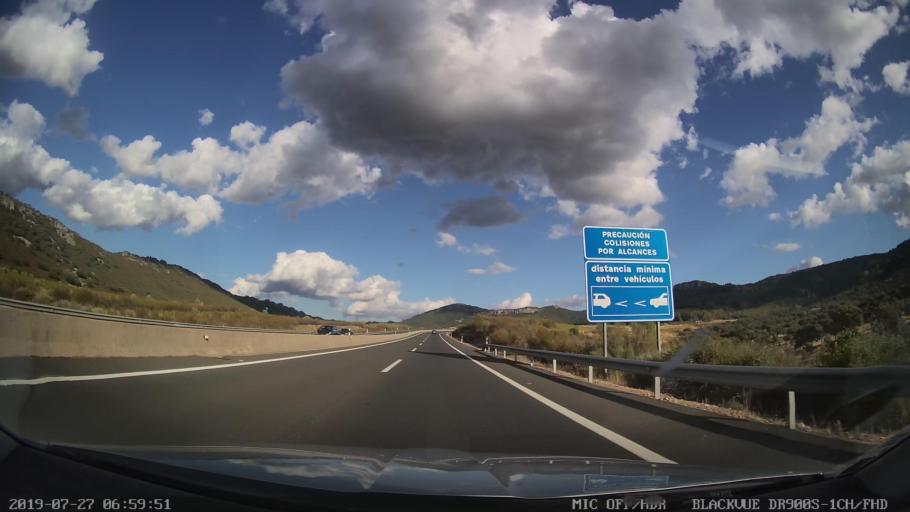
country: ES
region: Extremadura
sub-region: Provincia de Caceres
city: Higuera
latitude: 39.7107
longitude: -5.6943
